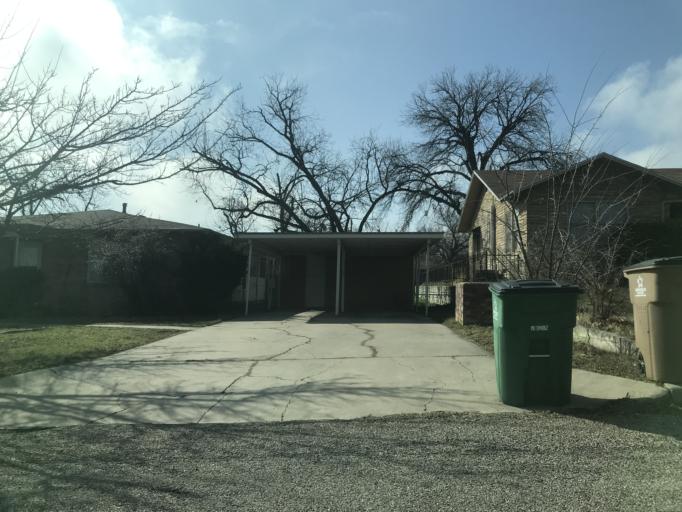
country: US
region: Texas
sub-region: Tom Green County
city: San Angelo
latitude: 31.4535
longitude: -100.4438
